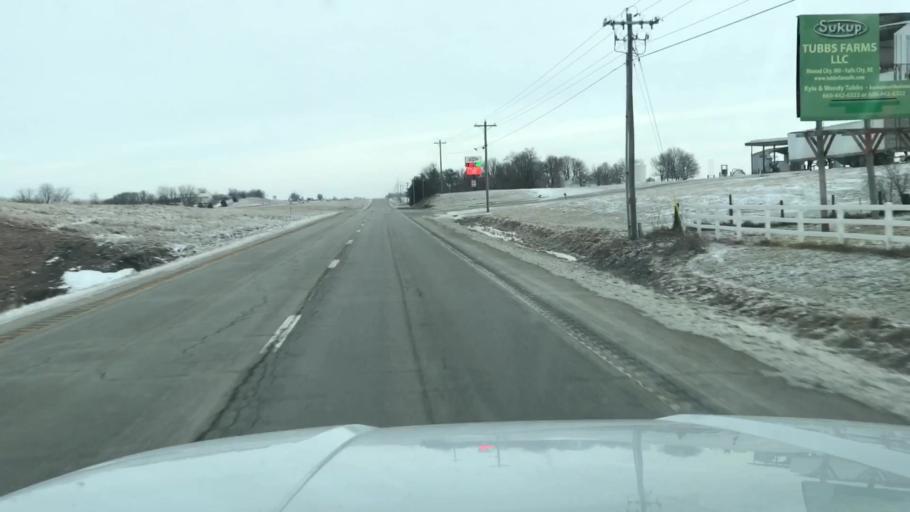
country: US
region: Missouri
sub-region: Andrew County
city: Savannah
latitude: 39.9987
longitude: -94.8798
